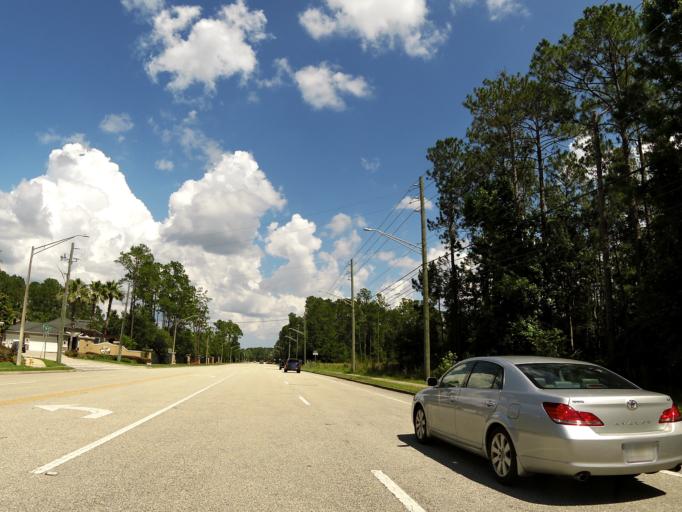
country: US
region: Florida
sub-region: Saint Johns County
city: Fruit Cove
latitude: 30.1525
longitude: -81.5850
